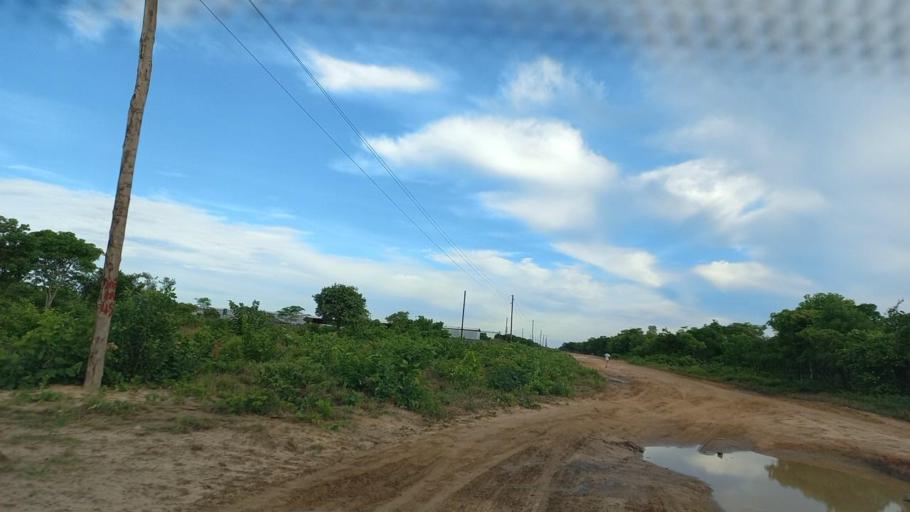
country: ZM
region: North-Western
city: Kabompo
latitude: -13.4175
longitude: 24.3202
